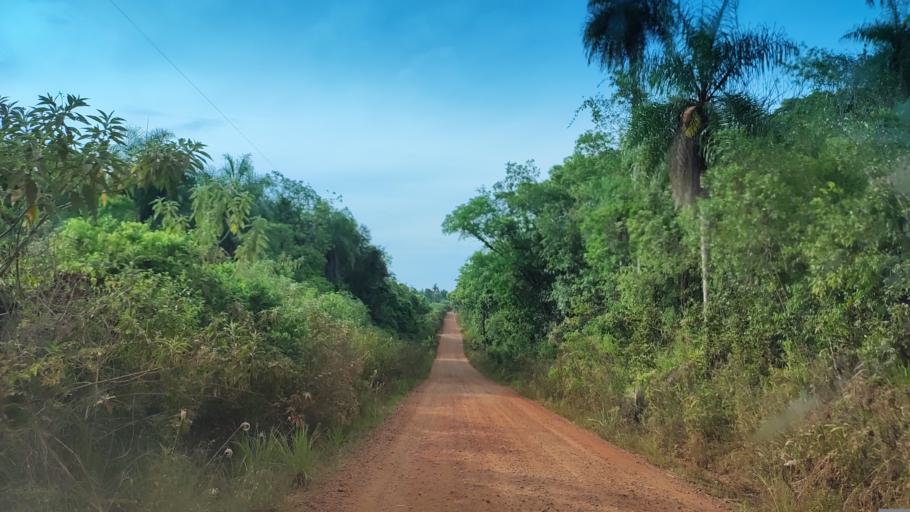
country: AR
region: Misiones
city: Gobernador Roca
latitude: -27.1604
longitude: -55.5203
